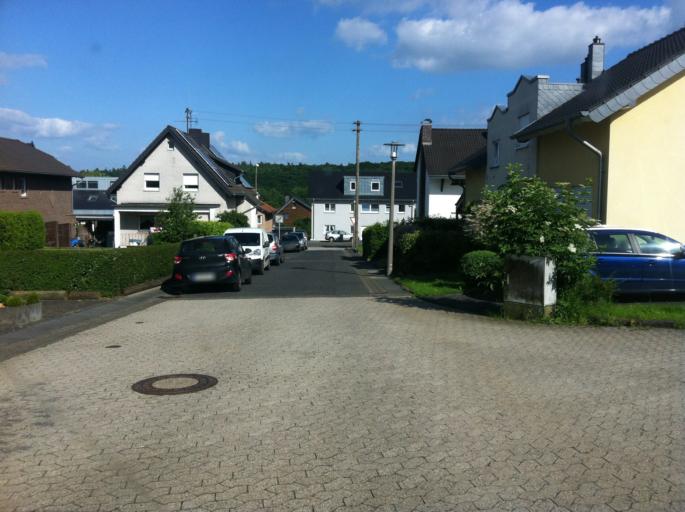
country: DE
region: North Rhine-Westphalia
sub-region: Regierungsbezirk Koln
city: Rheinbach
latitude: 50.6025
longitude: 6.9326
